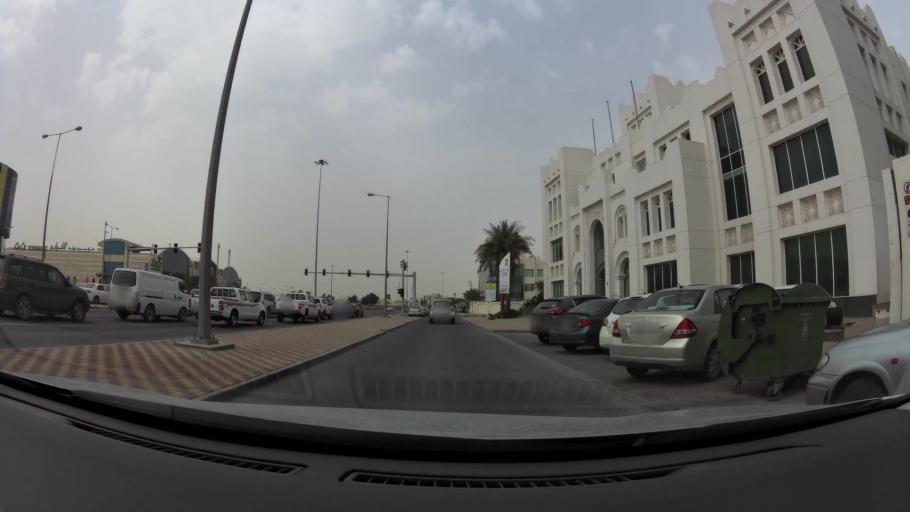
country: QA
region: Baladiyat ad Dawhah
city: Doha
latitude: 25.2558
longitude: 51.5468
